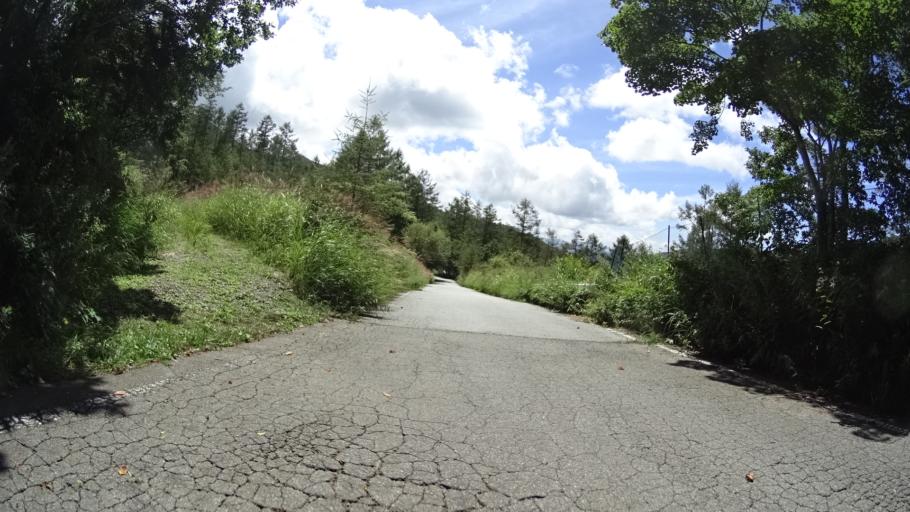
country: JP
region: Yamanashi
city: Enzan
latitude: 35.7274
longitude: 138.8429
